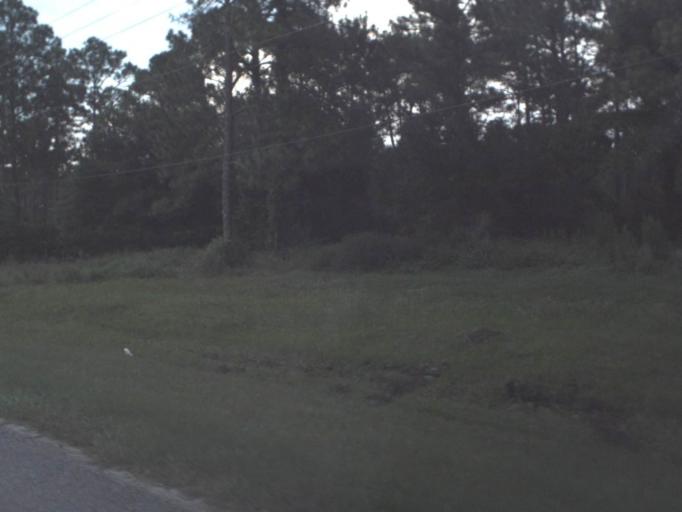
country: US
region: Florida
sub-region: Saint Johns County
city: Villano Beach
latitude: 29.9980
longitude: -81.3788
